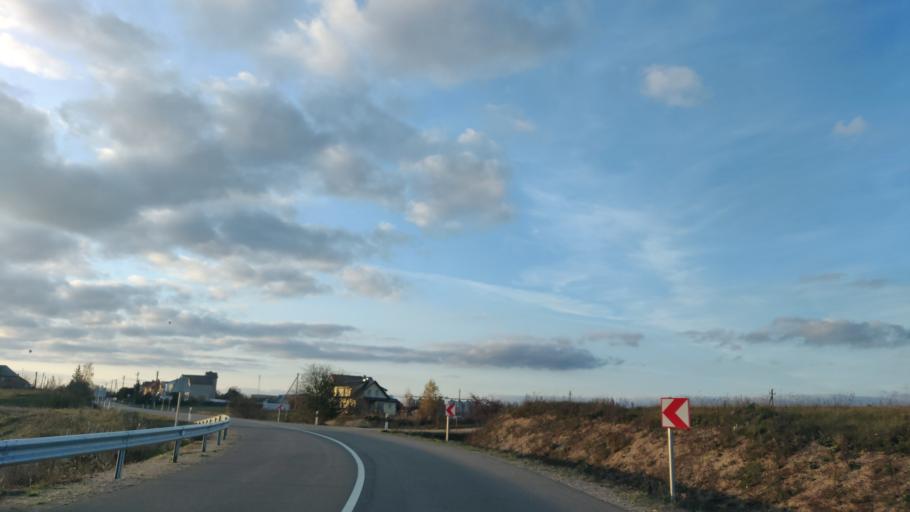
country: LT
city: Trakai
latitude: 54.6093
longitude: 24.9924
